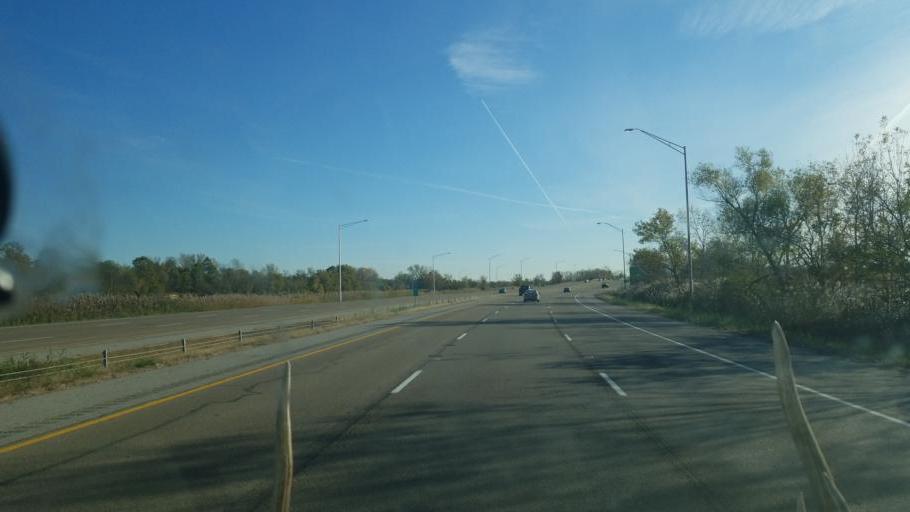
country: US
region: Illinois
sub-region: Saint Clair County
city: Fairmont City
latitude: 38.6625
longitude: -90.1006
